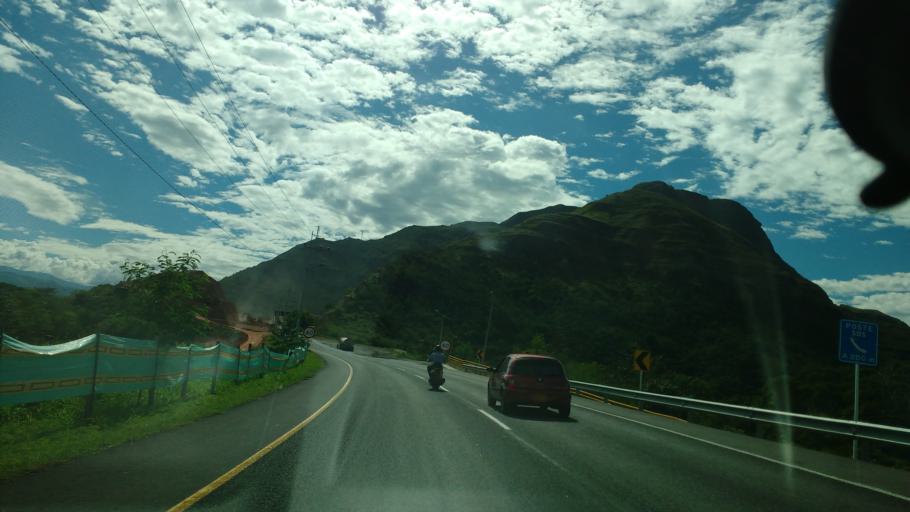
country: CO
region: Tolima
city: Valle de San Juan
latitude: 4.2803
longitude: -75.0153
